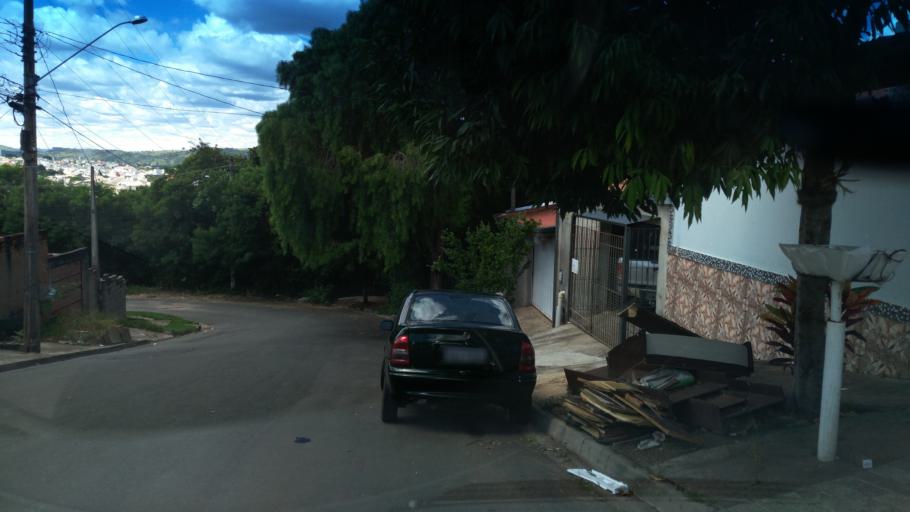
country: BR
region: Sao Paulo
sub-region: Valinhos
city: Valinhos
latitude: -22.9527
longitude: -47.0066
